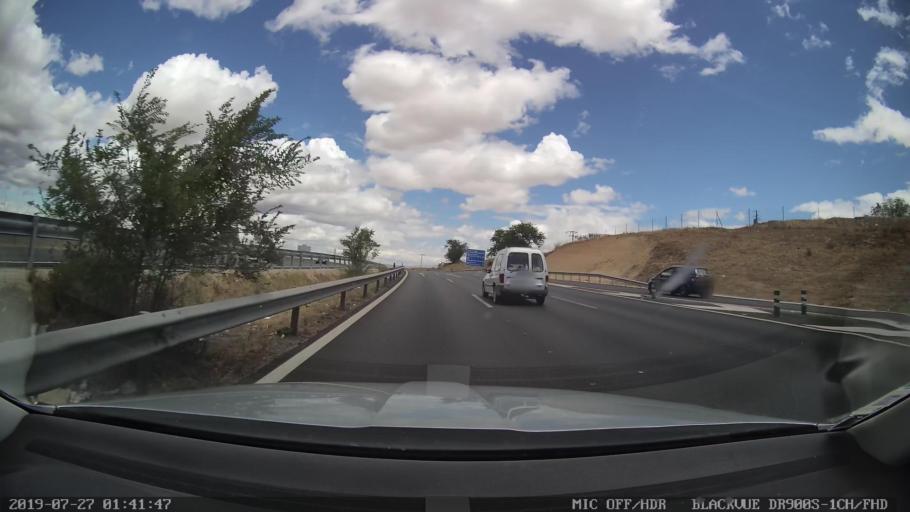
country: ES
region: Madrid
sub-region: Provincia de Madrid
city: Arroyomolinos
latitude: 40.3062
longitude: -3.9062
